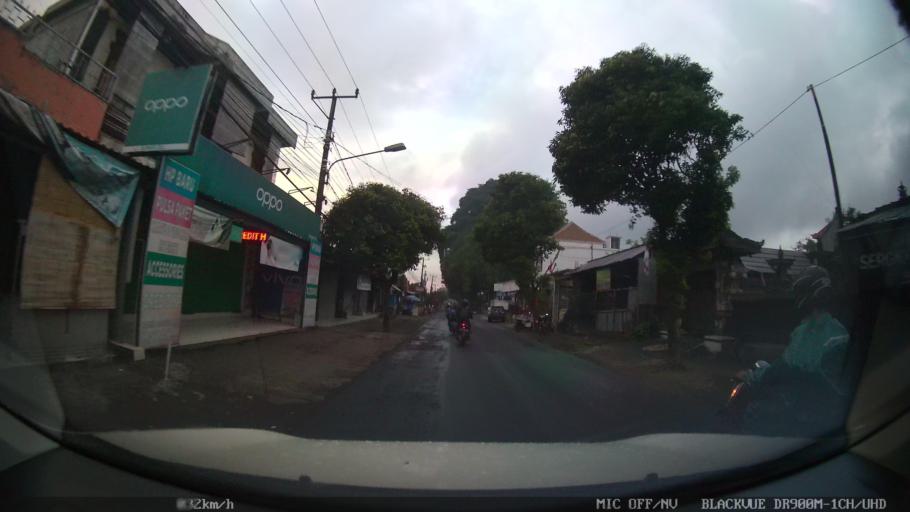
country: ID
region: Bali
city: Banjar Parekan
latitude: -8.5715
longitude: 115.2190
